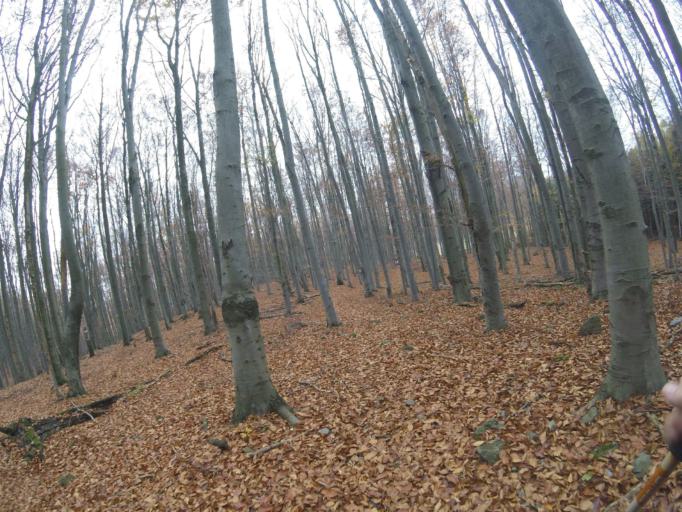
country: HU
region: Borsod-Abauj-Zemplen
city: Gonc
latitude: 48.4181
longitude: 21.3875
